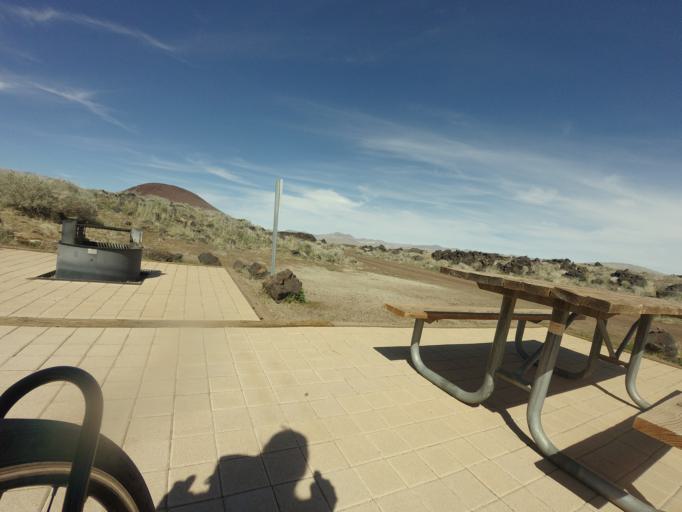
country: US
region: California
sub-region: Kern County
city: Inyokern
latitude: 35.9747
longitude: -117.9116
